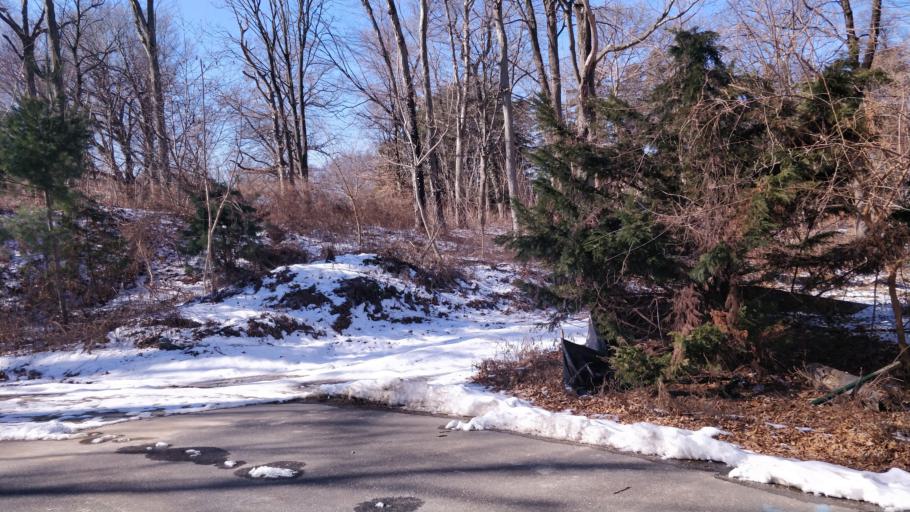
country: US
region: New York
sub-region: Nassau County
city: Old Westbury
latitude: 40.7871
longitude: -73.5904
